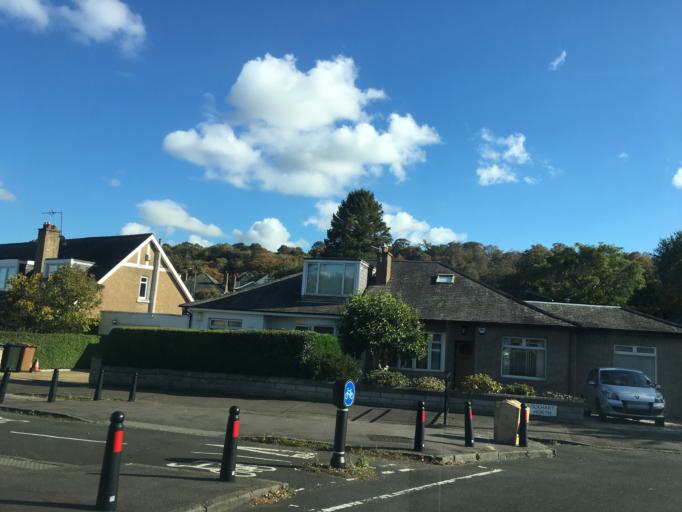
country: GB
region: Scotland
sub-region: Edinburgh
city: Colinton
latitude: 55.9234
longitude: -3.2391
